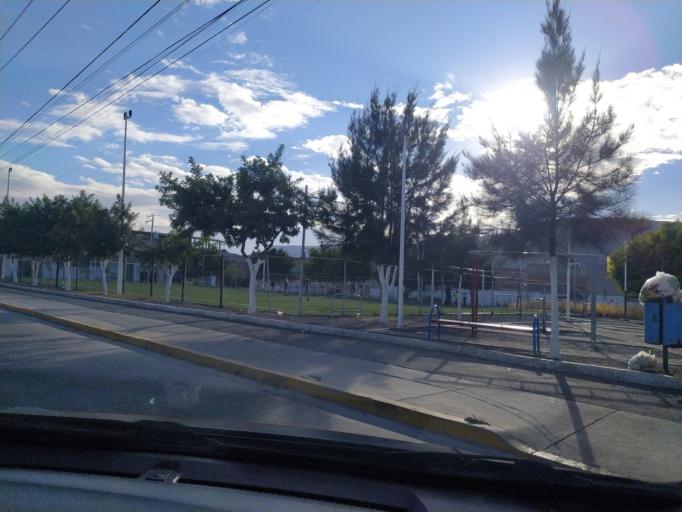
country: MX
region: Guanajuato
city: San Francisco del Rincon
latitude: 21.0219
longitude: -101.8767
